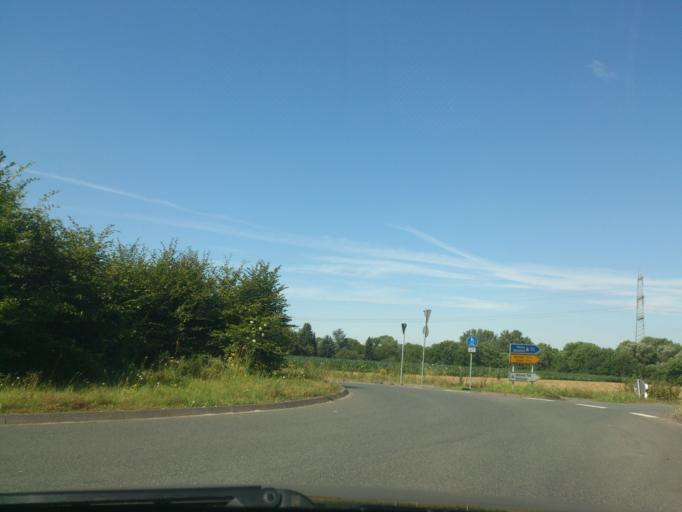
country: DE
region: North Rhine-Westphalia
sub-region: Regierungsbezirk Detmold
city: Paderborn
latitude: 51.6994
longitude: 8.7140
